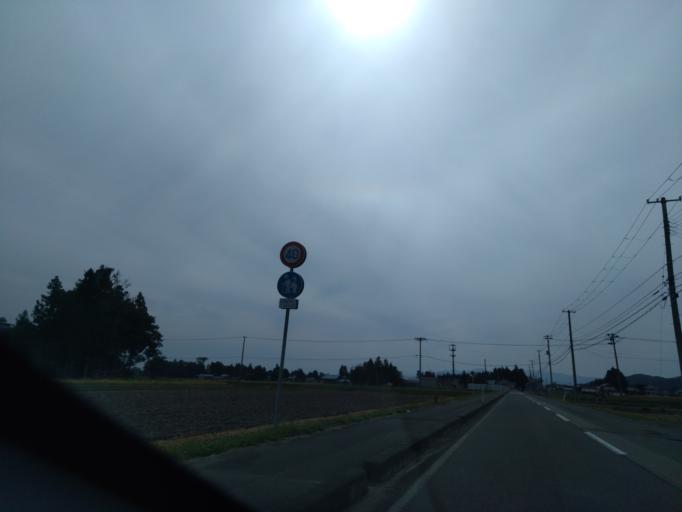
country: JP
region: Iwate
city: Hanamaki
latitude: 39.4416
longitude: 141.0832
